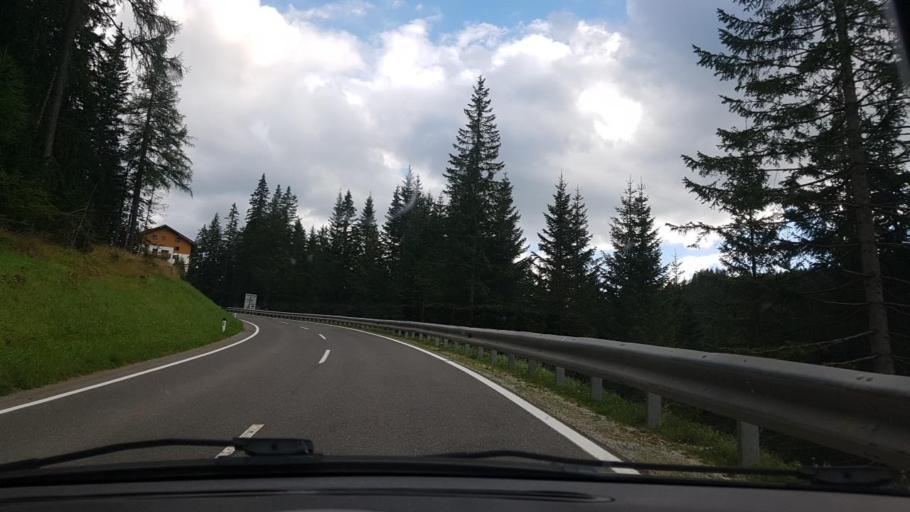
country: AT
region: Salzburg
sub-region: Politischer Bezirk Tamsweg
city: Sankt Michael im Lungau
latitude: 47.0624
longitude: 13.6131
